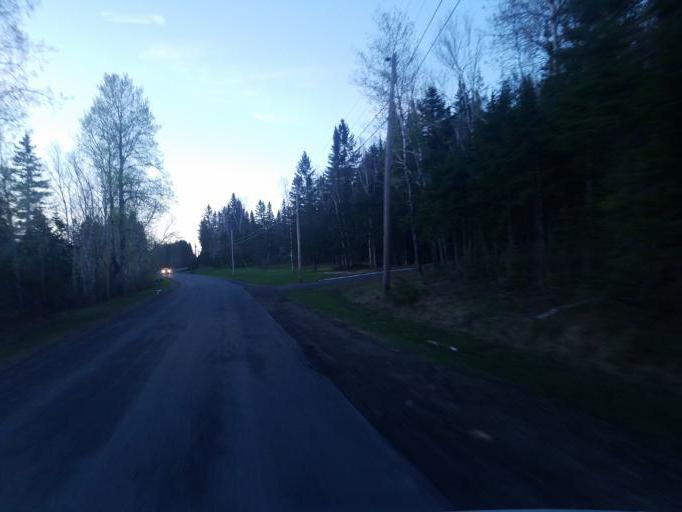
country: US
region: Maine
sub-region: Aroostook County
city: Caribou
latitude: 46.8672
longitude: -68.0709
